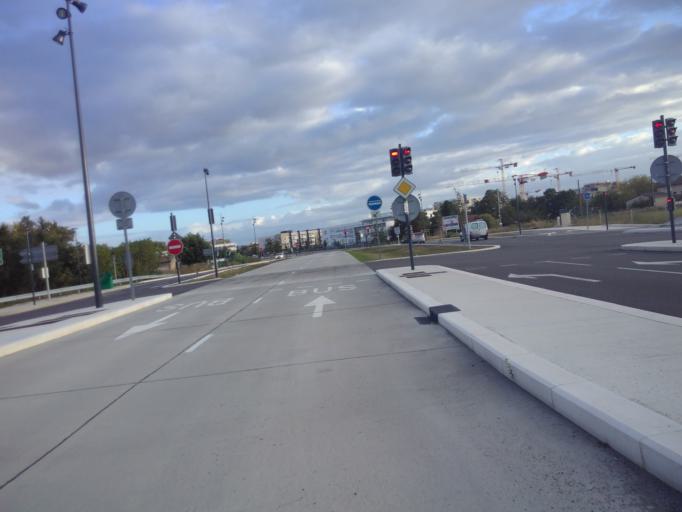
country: FR
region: Midi-Pyrenees
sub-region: Departement de la Haute-Garonne
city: L'Union
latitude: 43.6461
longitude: 1.4549
